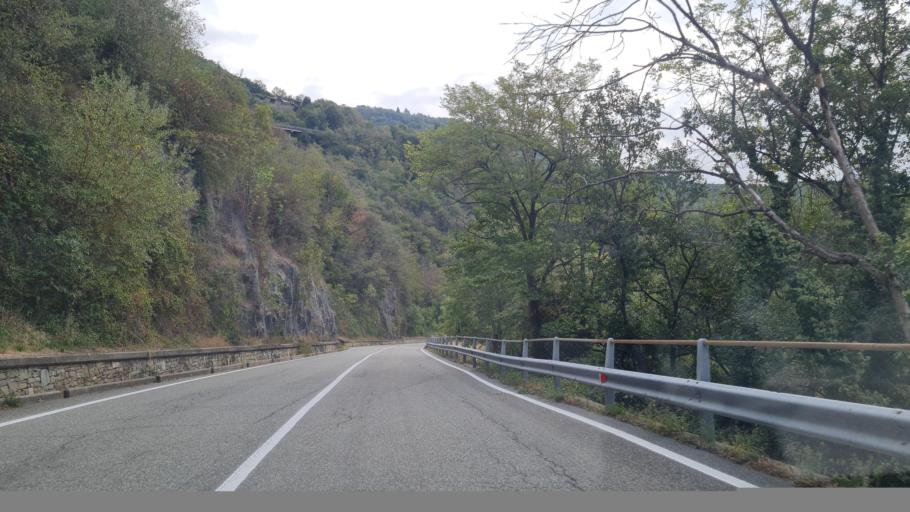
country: IT
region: Piedmont
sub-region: Provincia di Torino
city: Borgofranco d'Ivrea
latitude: 45.5193
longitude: 7.8686
